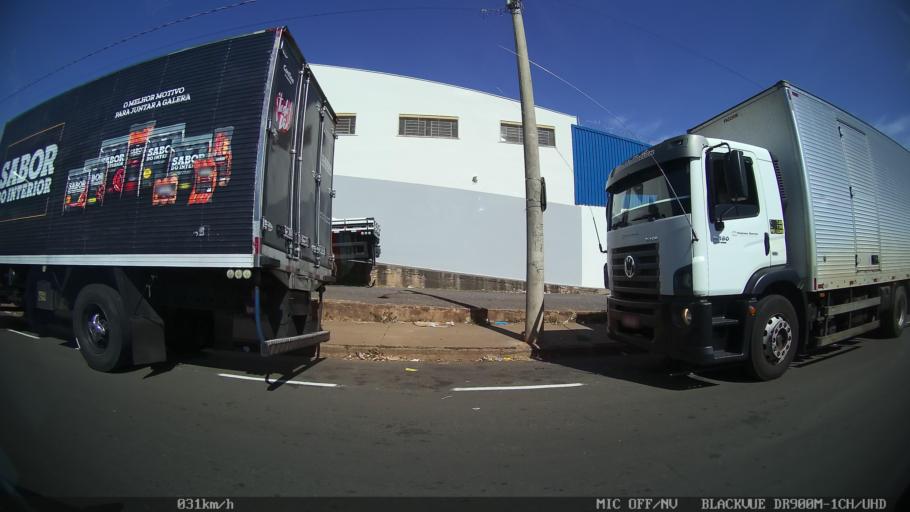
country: BR
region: Sao Paulo
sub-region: Sao Jose Do Rio Preto
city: Sao Jose do Rio Preto
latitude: -20.7729
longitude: -49.4146
